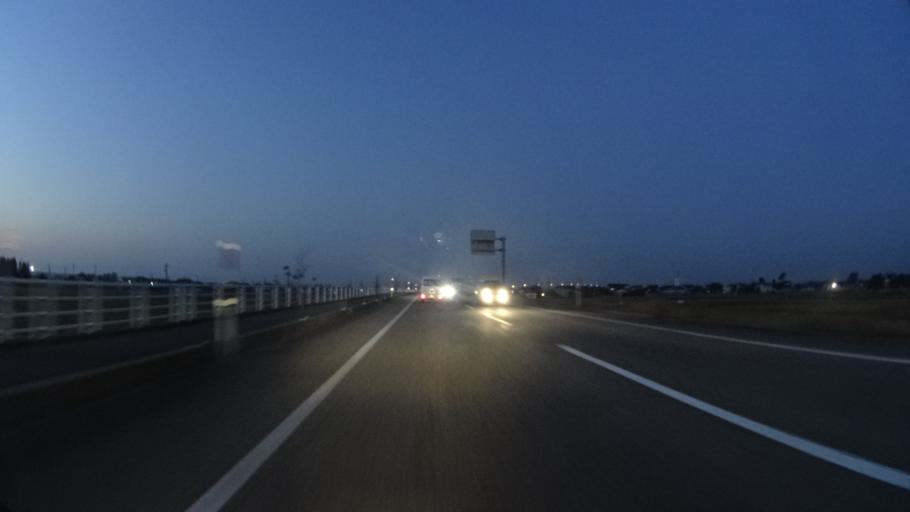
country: JP
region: Toyama
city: Nyuzen
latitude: 36.8944
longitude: 137.4441
